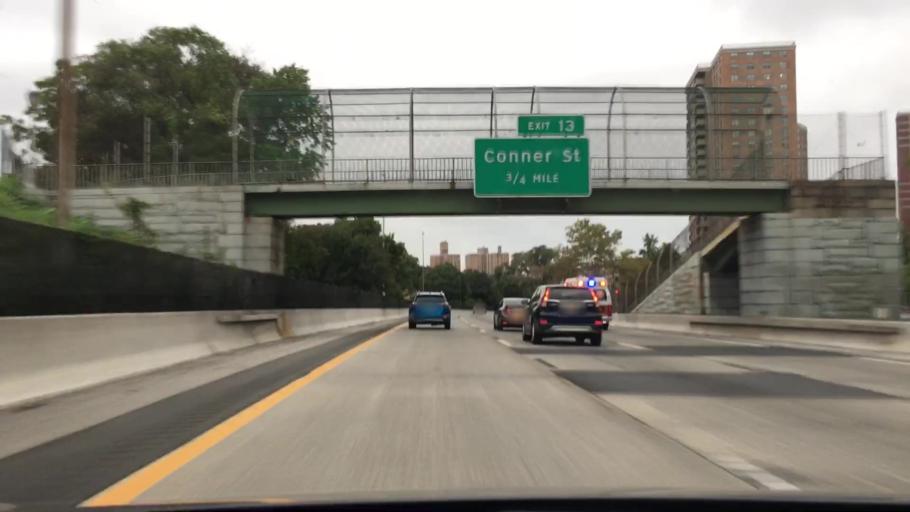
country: US
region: New York
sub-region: Bronx
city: Eastchester
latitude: 40.8747
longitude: -73.8343
